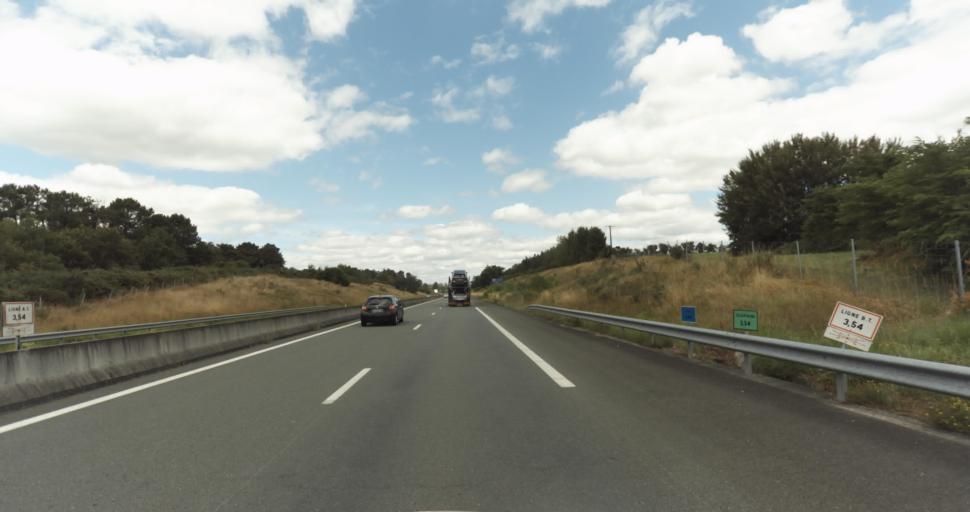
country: FR
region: Aquitaine
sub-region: Departement de la Gironde
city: Bazas
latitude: 44.4997
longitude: -0.1989
